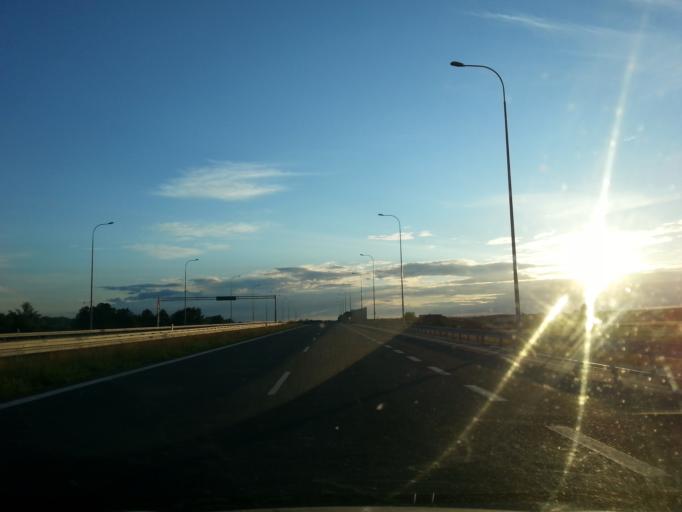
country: PL
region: Greater Poland Voivodeship
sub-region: Powiat kepinski
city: Kepno
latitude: 51.3165
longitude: 17.9987
